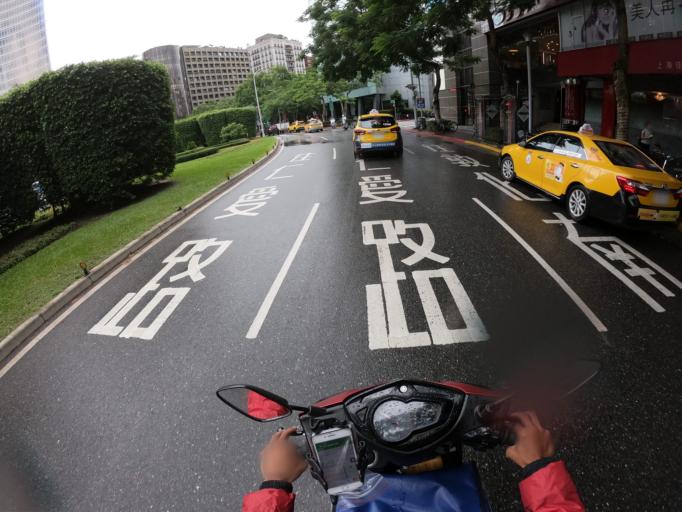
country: TW
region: Taipei
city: Taipei
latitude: 25.0375
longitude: 121.5480
